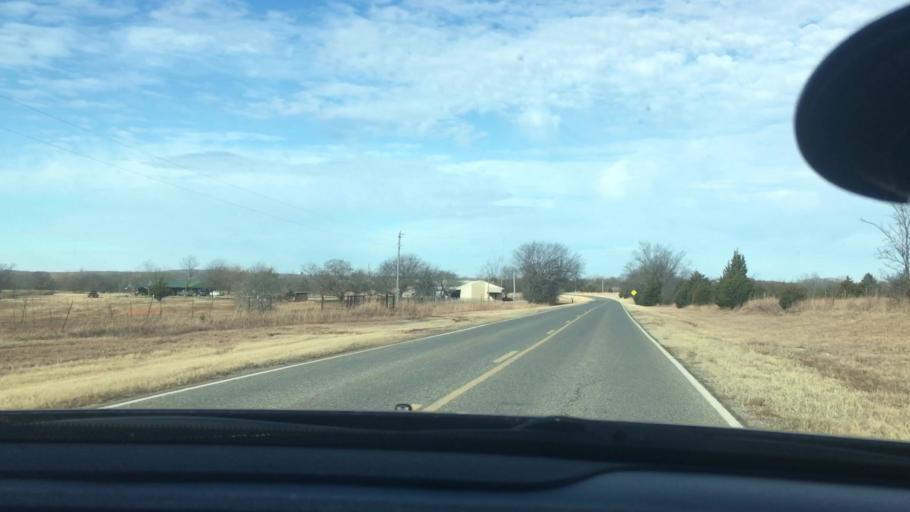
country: US
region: Oklahoma
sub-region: Seminole County
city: Konawa
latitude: 34.9820
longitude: -96.7929
